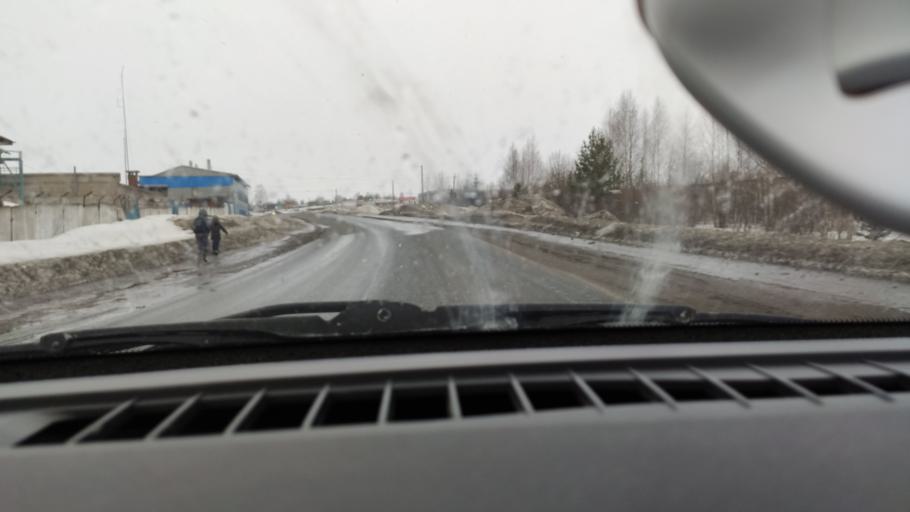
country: RU
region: Perm
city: Nytva
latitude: 57.9489
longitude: 55.3591
